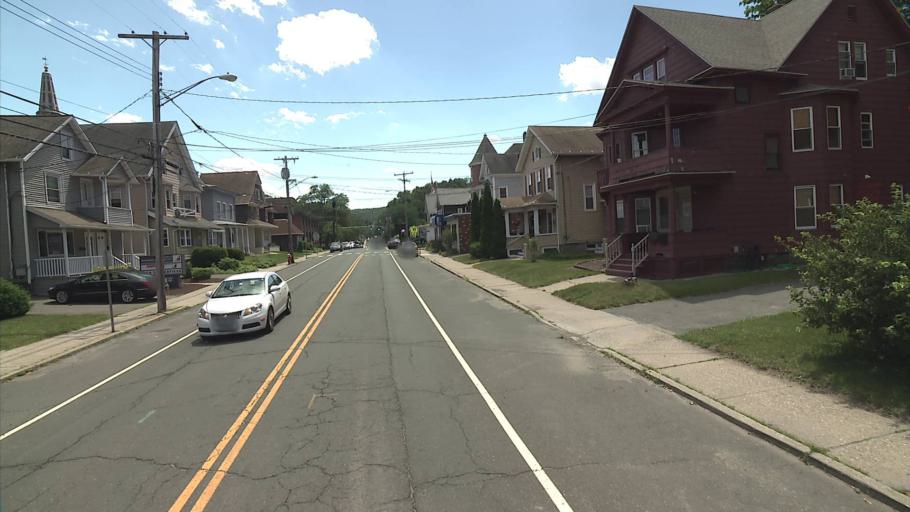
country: US
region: Connecticut
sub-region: New Haven County
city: Naugatuck
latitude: 41.4923
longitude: -73.0562
